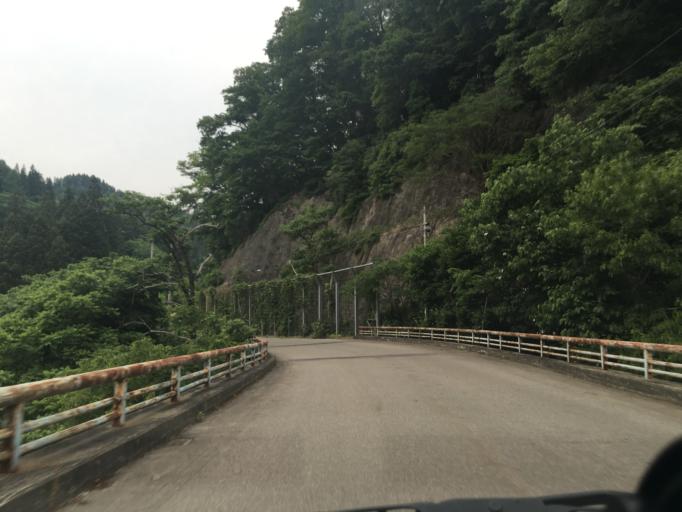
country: JP
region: Fukushima
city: Kitakata
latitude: 37.4905
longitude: 139.7366
